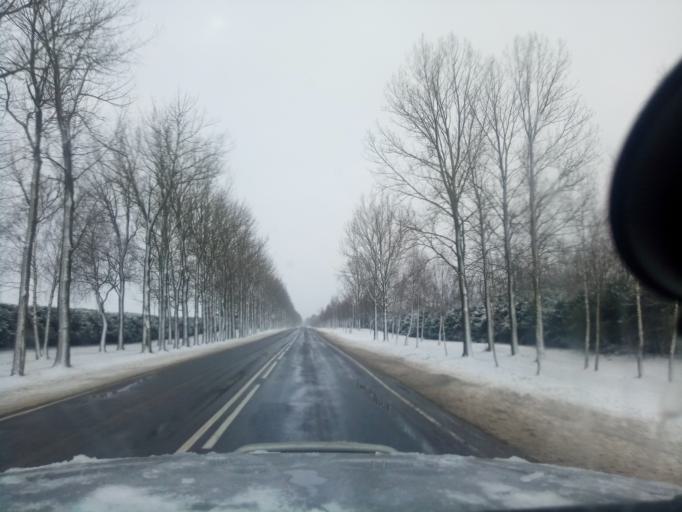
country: BY
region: Minsk
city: Haradzyeya
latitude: 53.3482
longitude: 26.5180
